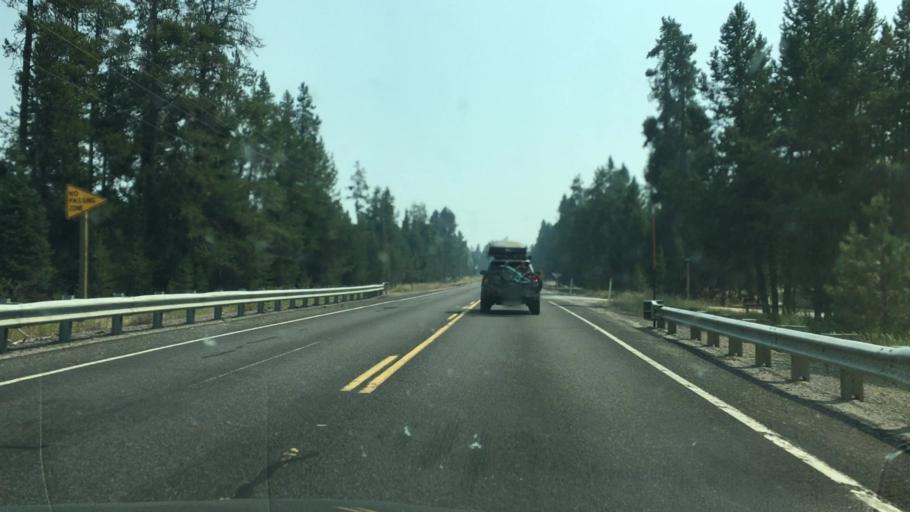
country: US
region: Idaho
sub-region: Valley County
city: Cascade
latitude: 44.4115
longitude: -115.9998
